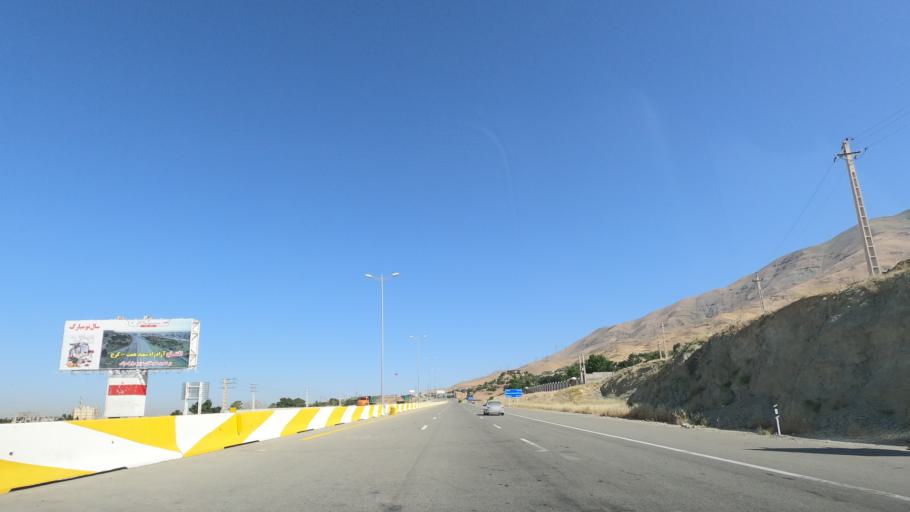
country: IR
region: Tehran
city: Shahr-e Qods
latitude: 35.7575
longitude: 51.0787
